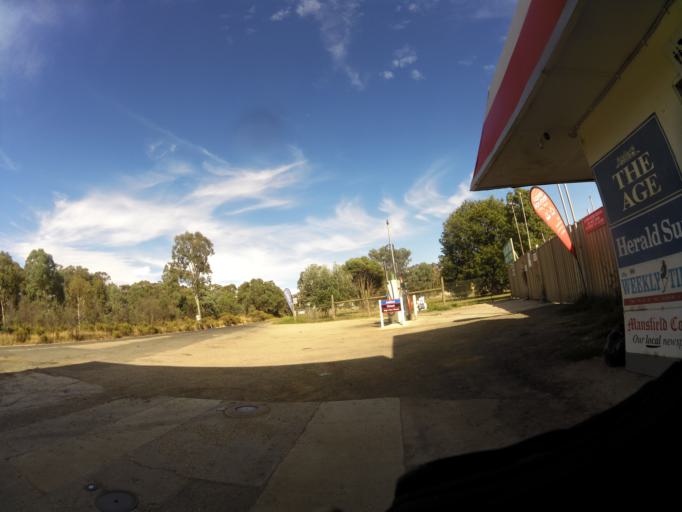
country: AU
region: Victoria
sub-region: Murrindindi
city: Alexandra
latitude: -36.9773
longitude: 145.7106
